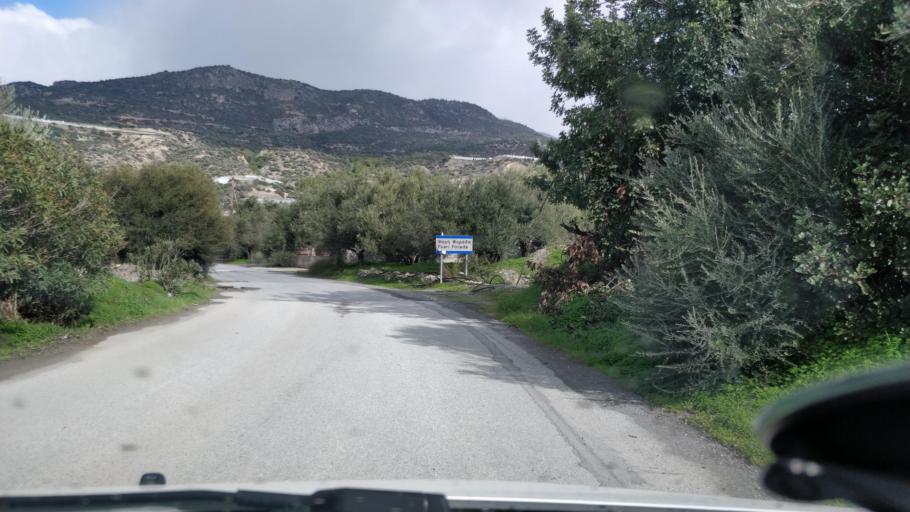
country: GR
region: Crete
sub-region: Nomos Lasithiou
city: Gra Liyia
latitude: 34.9929
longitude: 25.5042
